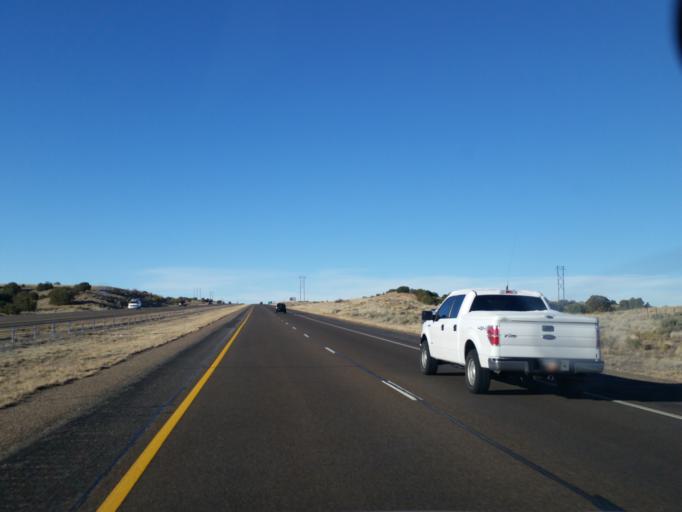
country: US
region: New Mexico
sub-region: Sandoval County
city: Santo Domingo Pueblo
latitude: 35.4833
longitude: -106.2731
